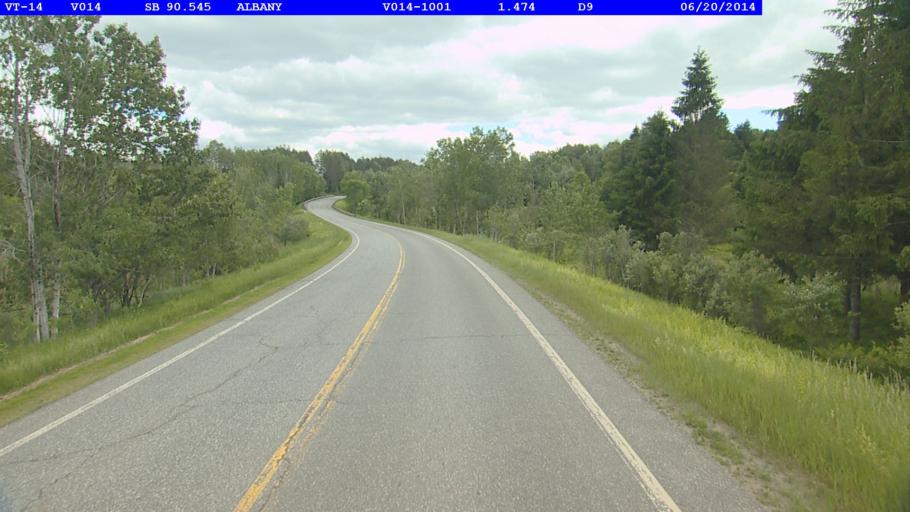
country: US
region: Vermont
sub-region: Caledonia County
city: Hardwick
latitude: 44.7228
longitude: -72.3839
